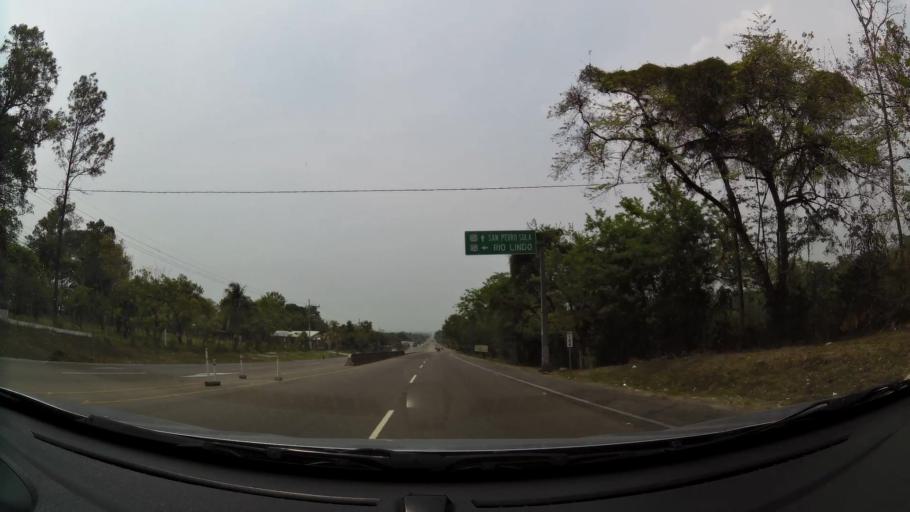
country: HN
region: Cortes
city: Oropendolas
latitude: 15.0318
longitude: -87.9278
